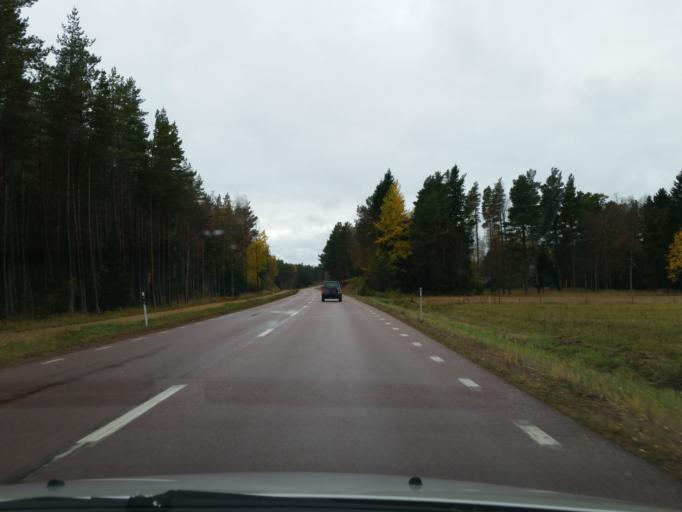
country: AX
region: Alands landsbygd
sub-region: Lemland
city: Lemland
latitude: 60.0749
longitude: 20.1725
